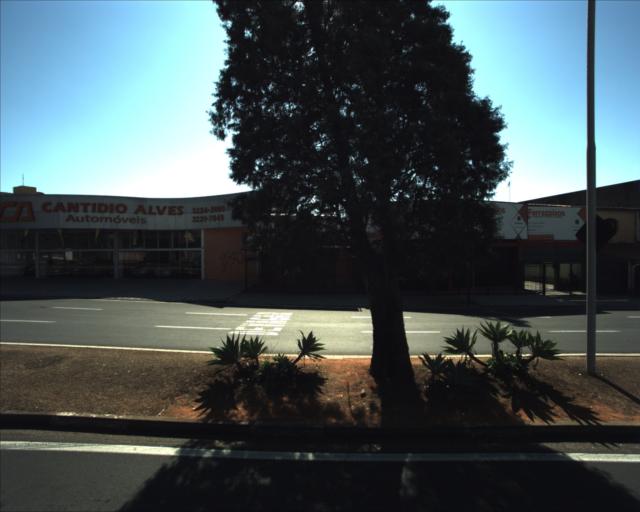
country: BR
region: Sao Paulo
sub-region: Sorocaba
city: Sorocaba
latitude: -23.5071
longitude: -47.4532
